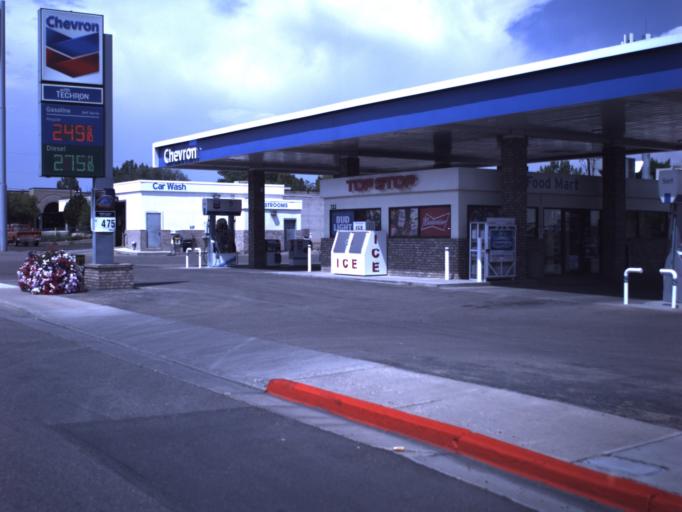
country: US
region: Utah
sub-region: Uintah County
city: Vernal
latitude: 40.4556
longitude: -109.5416
